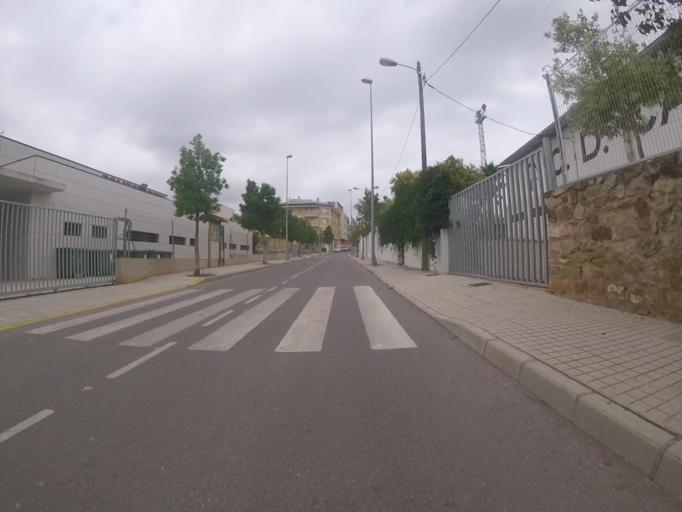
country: ES
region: Valencia
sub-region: Provincia de Castello
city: Cabanes
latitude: 40.1530
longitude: 0.0473
